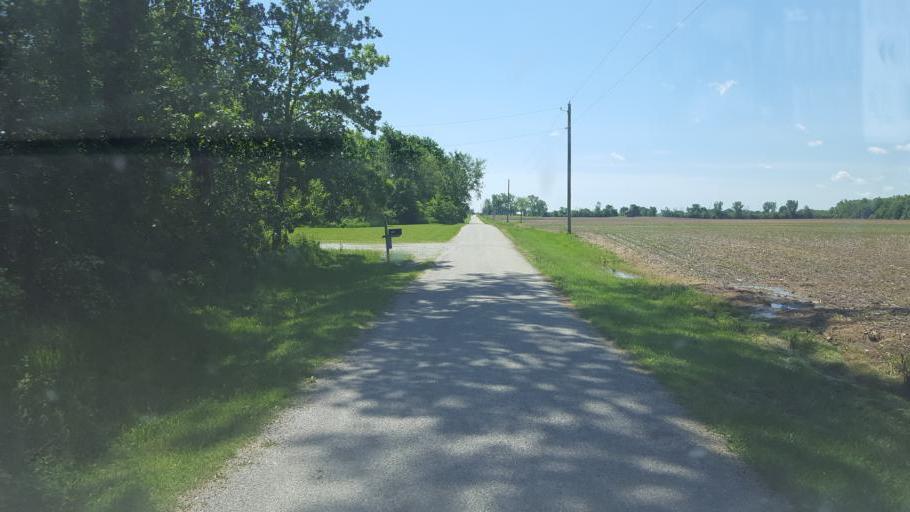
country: US
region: Ohio
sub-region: Union County
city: Richwood
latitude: 40.5809
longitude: -83.3959
